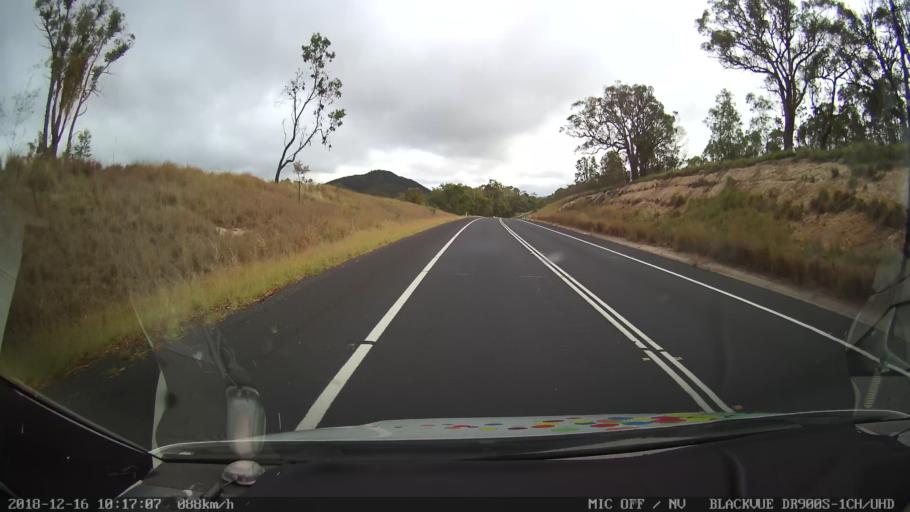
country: AU
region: New South Wales
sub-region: Tenterfield Municipality
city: Carrolls Creek
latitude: -29.2596
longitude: 151.9889
